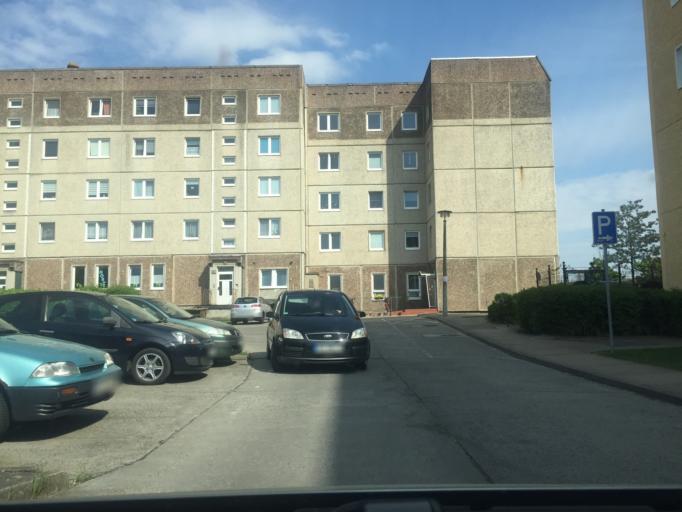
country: DE
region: Mecklenburg-Vorpommern
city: Torgelow
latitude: 53.6318
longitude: 14.0104
